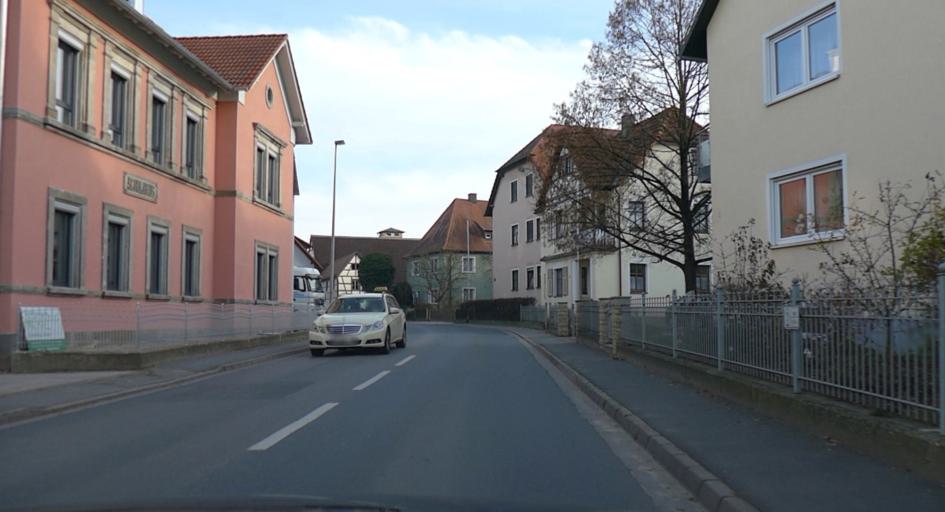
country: DE
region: Bavaria
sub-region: Upper Franconia
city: Poxdorf
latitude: 49.6658
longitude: 11.0697
